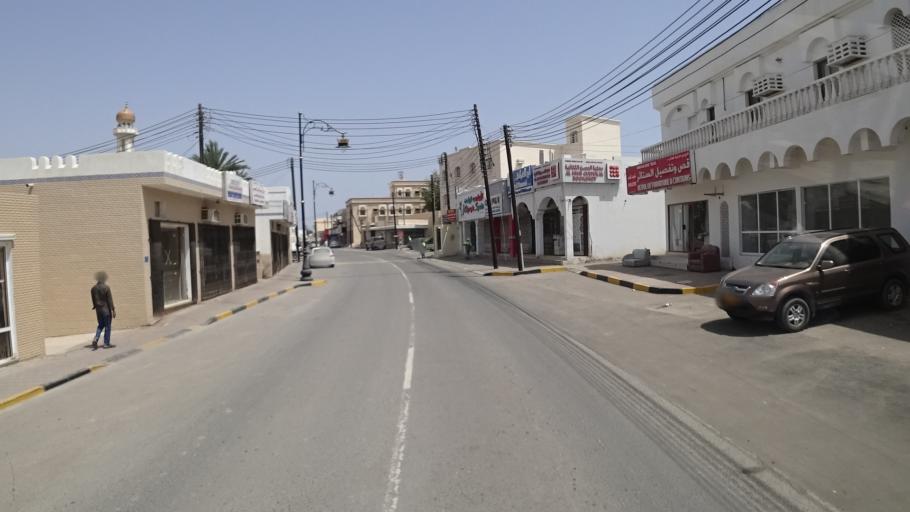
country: OM
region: Muhafazat Masqat
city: Muscat
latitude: 23.2620
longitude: 58.9159
